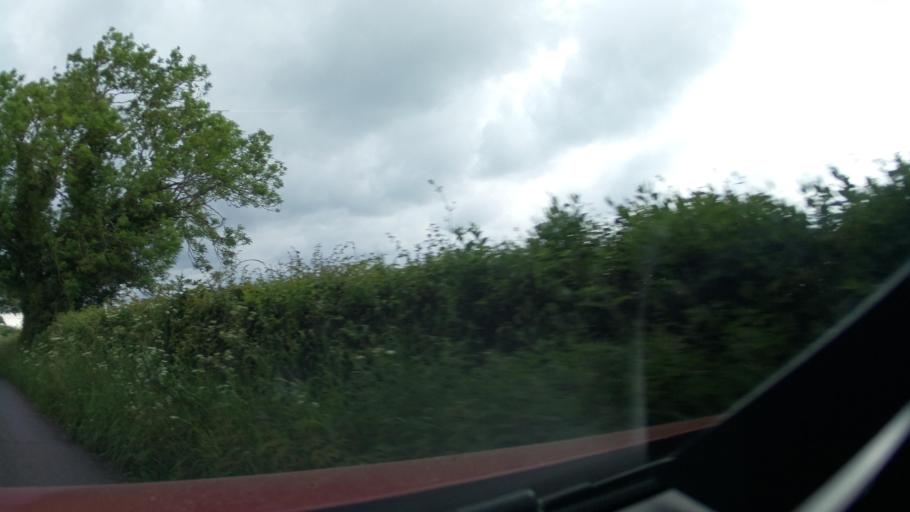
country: GB
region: England
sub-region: South Gloucestershire
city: Pucklechurch
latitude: 51.4651
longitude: -2.4208
